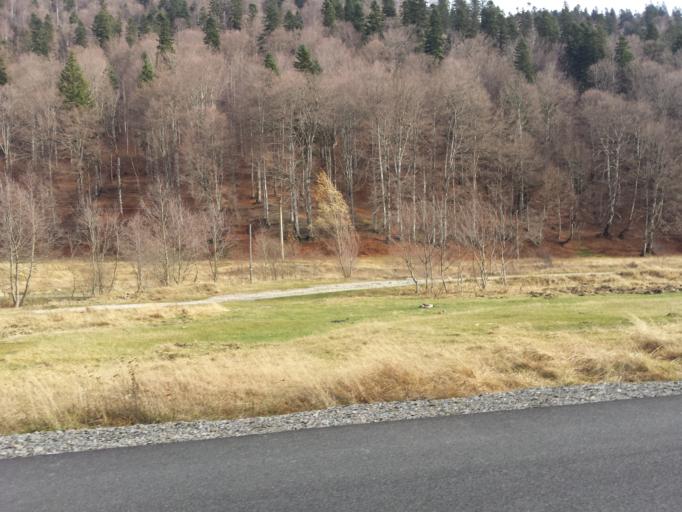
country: RO
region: Prahova
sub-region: Oras Azuga
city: Azuga
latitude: 45.4414
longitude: 25.5253
